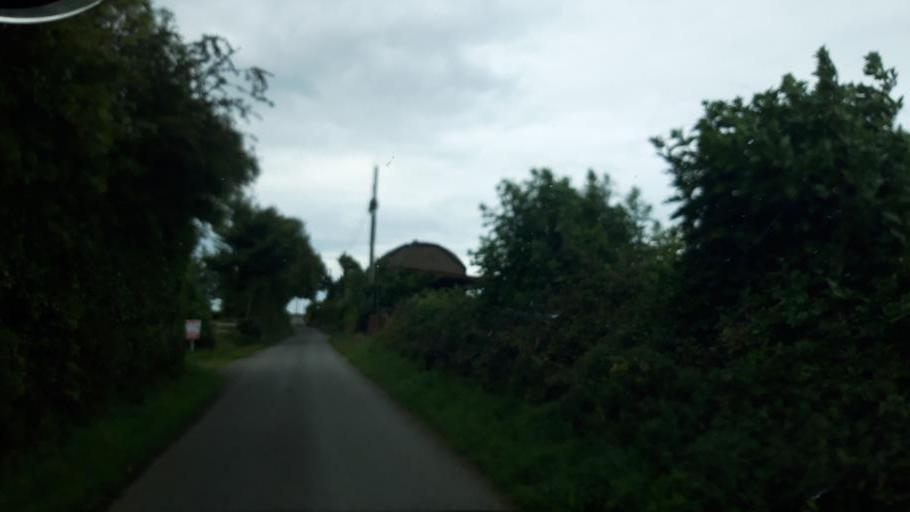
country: IE
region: Leinster
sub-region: Kilkenny
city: Ballyragget
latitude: 52.7924
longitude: -7.3328
